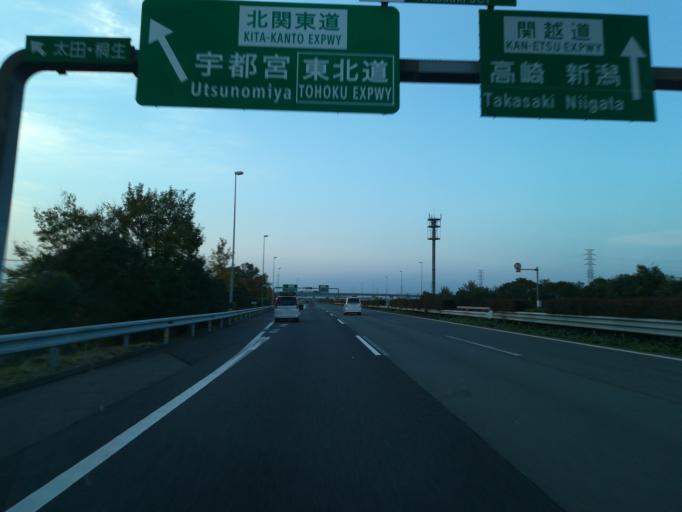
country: JP
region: Gunma
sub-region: Sawa-gun
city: Tamamura
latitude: 36.3178
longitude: 139.0805
